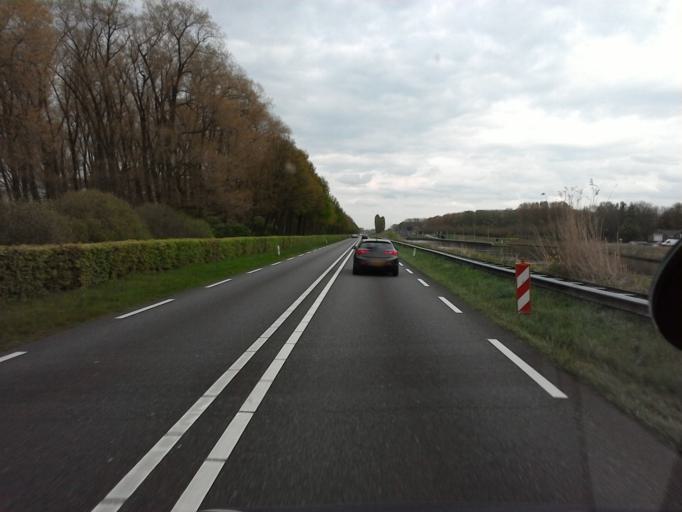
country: NL
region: North Brabant
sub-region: Gemeente Schijndel
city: Schijndel
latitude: 51.6511
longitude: 5.4357
